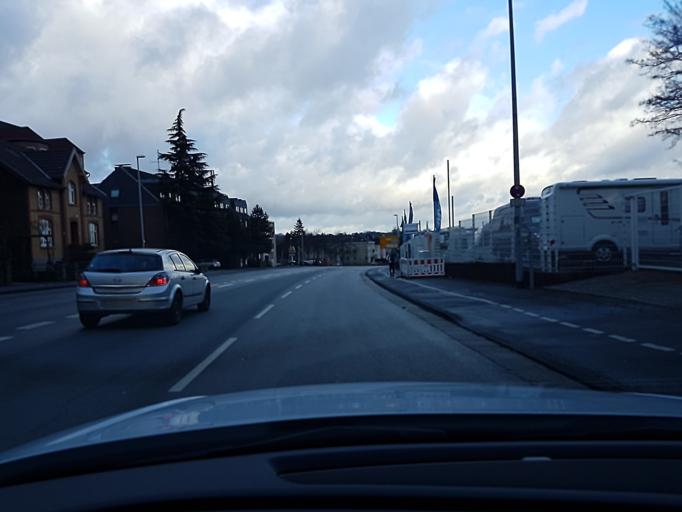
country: DE
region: North Rhine-Westphalia
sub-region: Regierungsbezirk Dusseldorf
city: Muelheim (Ruhr)
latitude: 51.3990
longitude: 6.8761
